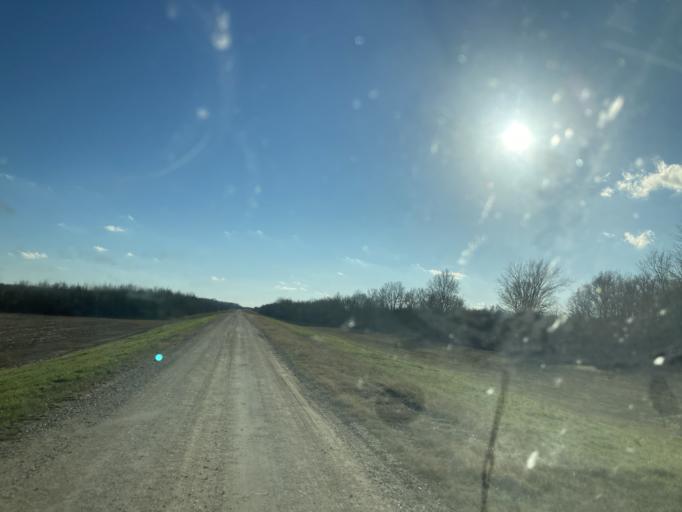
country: US
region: Mississippi
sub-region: Yazoo County
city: Yazoo City
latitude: 32.9318
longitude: -90.5483
